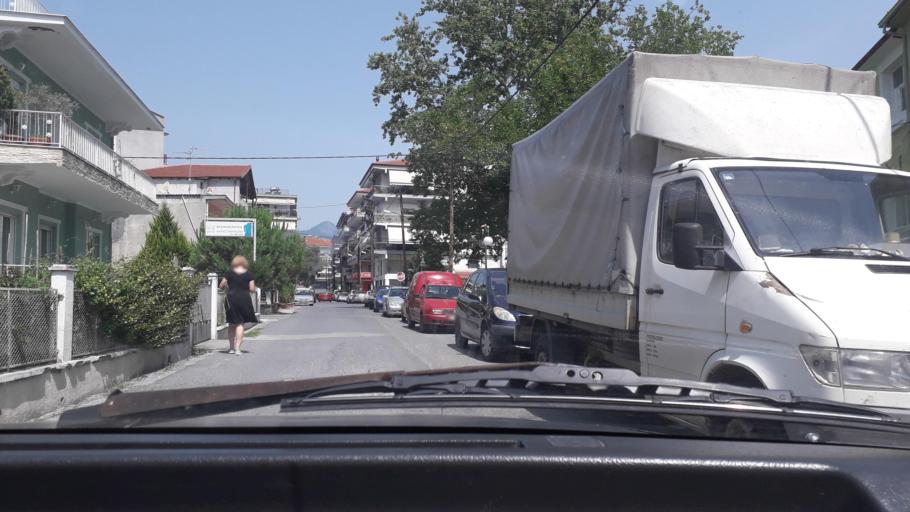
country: GR
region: Central Macedonia
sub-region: Nomos Pellis
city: Aridaia
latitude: 40.9725
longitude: 22.0620
